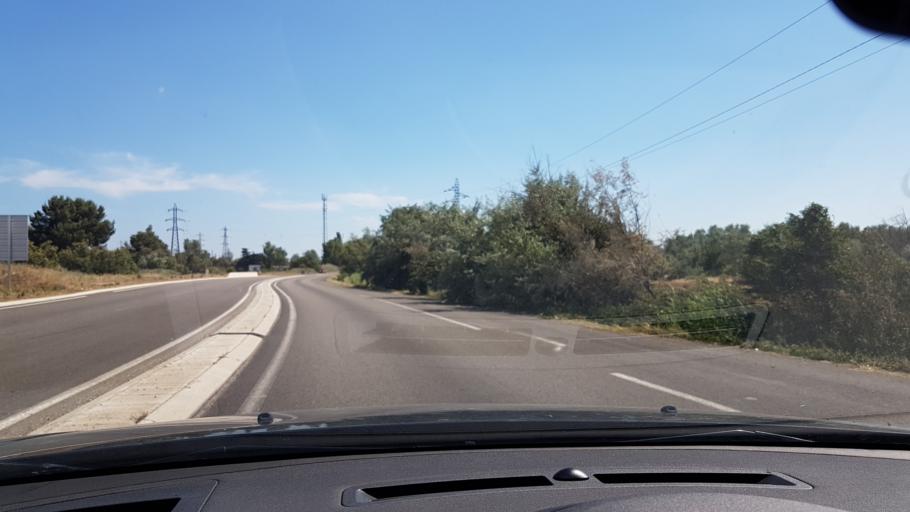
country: FR
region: Provence-Alpes-Cote d'Azur
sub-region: Departement des Bouches-du-Rhone
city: Port-Saint-Louis-du-Rhone
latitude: 43.4480
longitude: 4.8380
